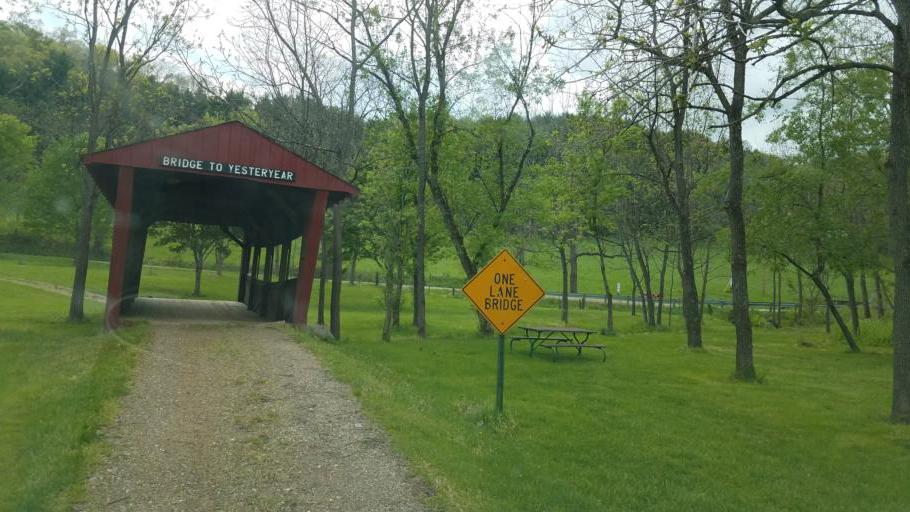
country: US
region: Ohio
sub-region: Ashland County
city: Loudonville
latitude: 40.5440
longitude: -82.2077
